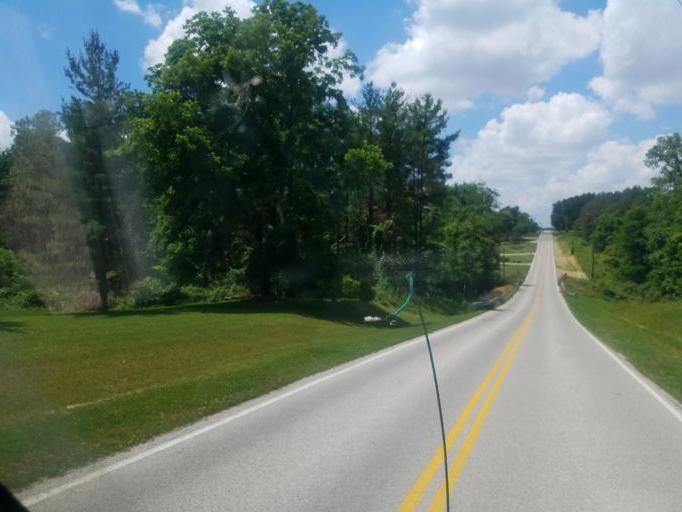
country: US
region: Ohio
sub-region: Huron County
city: Willard
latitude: 41.0794
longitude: -82.7277
